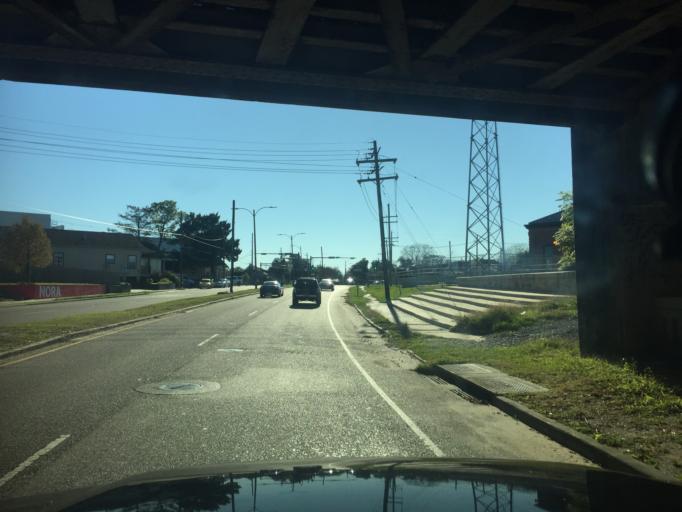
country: US
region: Louisiana
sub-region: Orleans Parish
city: New Orleans
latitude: 29.9887
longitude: -90.0670
